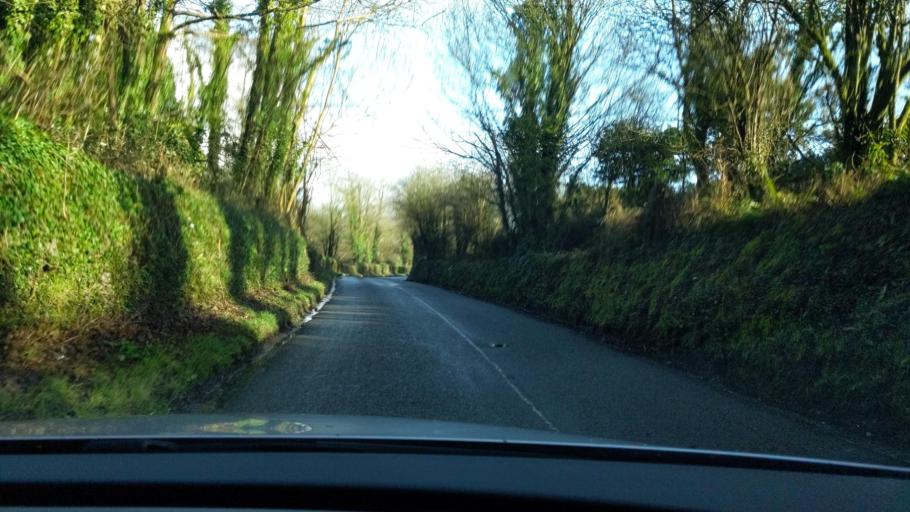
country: IE
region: Munster
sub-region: County Cork
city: Cork
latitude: 51.9264
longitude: -8.4989
